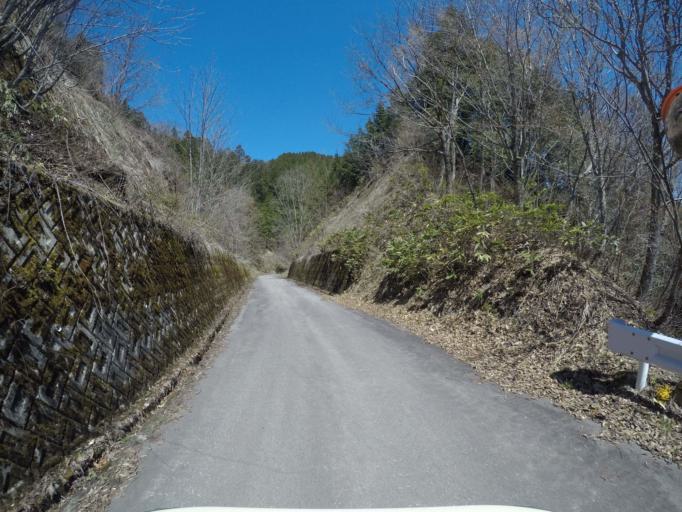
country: JP
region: Gifu
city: Takayama
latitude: 36.1498
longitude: 137.4223
